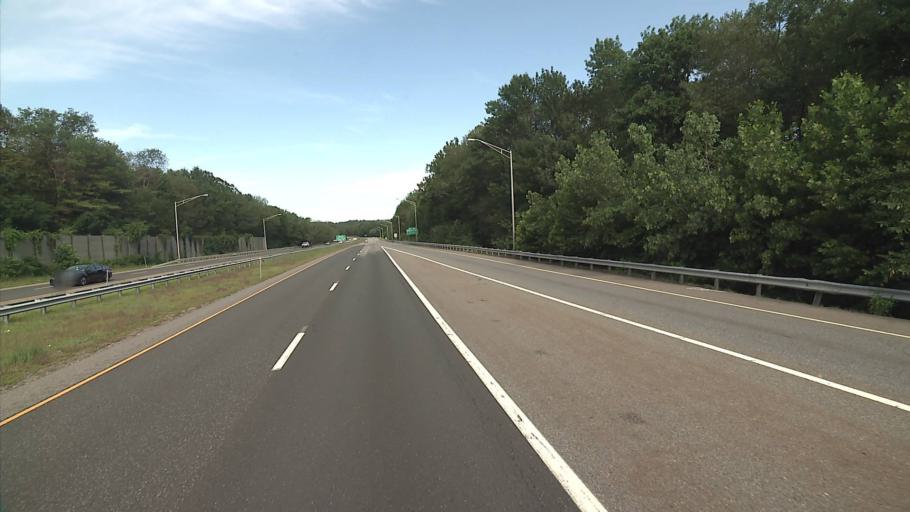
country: US
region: Connecticut
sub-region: New London County
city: Norwich
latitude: 41.5629
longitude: -72.1295
